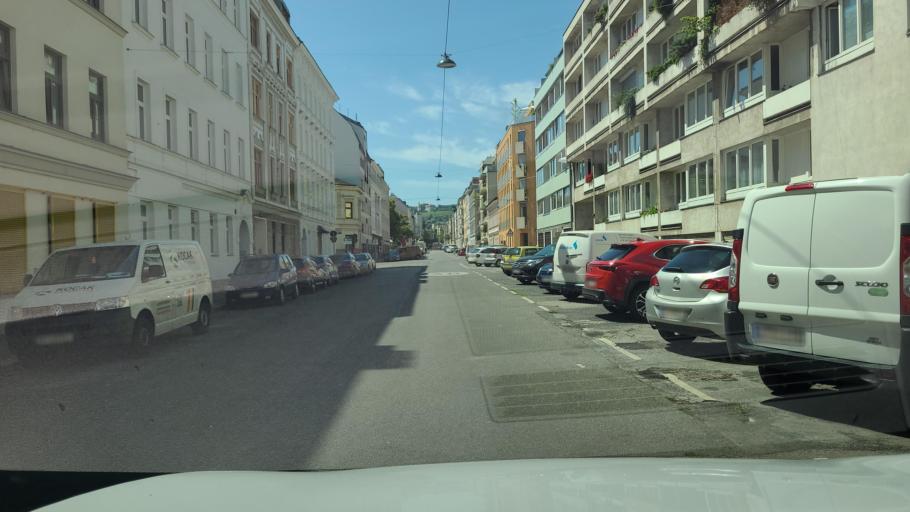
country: AT
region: Vienna
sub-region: Wien Stadt
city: Vienna
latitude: 48.2153
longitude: 16.3153
